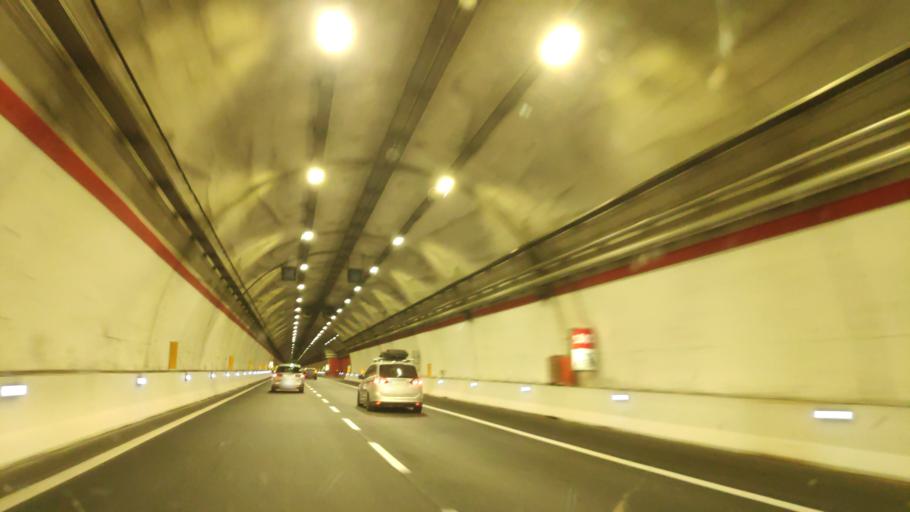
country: IT
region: Campania
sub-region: Provincia di Salerno
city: Petina
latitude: 40.5664
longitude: 15.3717
